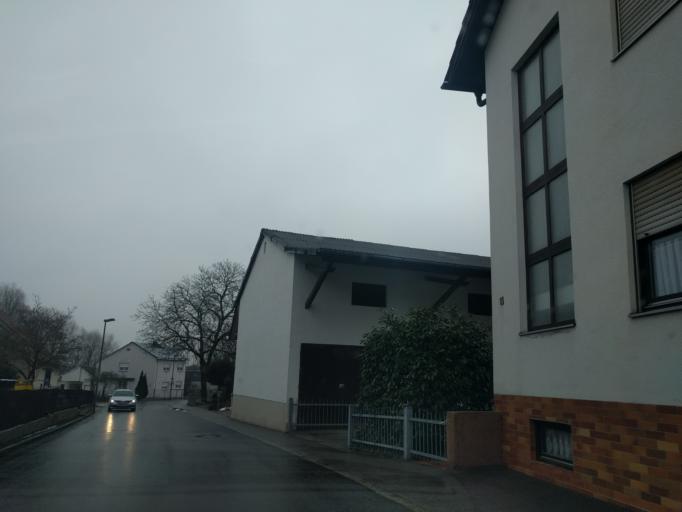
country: DE
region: Bavaria
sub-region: Lower Bavaria
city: Osterhofen
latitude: 48.7035
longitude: 13.0205
